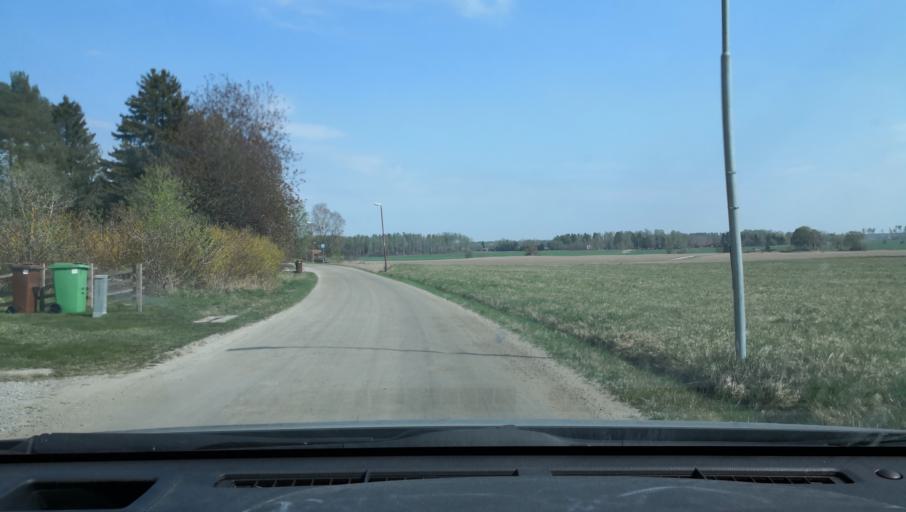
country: SE
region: Vaestmanland
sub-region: Vasteras
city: Skultuna
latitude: 59.7553
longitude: 16.4421
